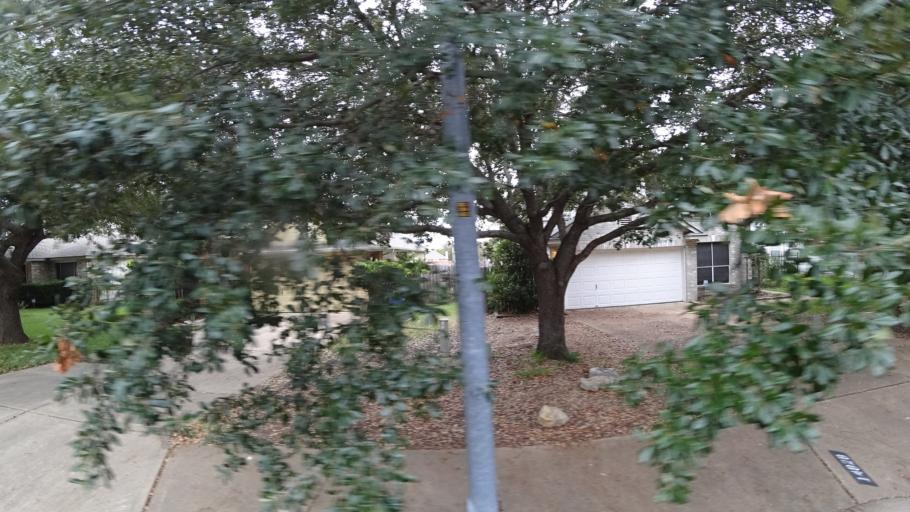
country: US
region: Texas
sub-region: Travis County
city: Wells Branch
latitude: 30.4496
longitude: -97.6879
